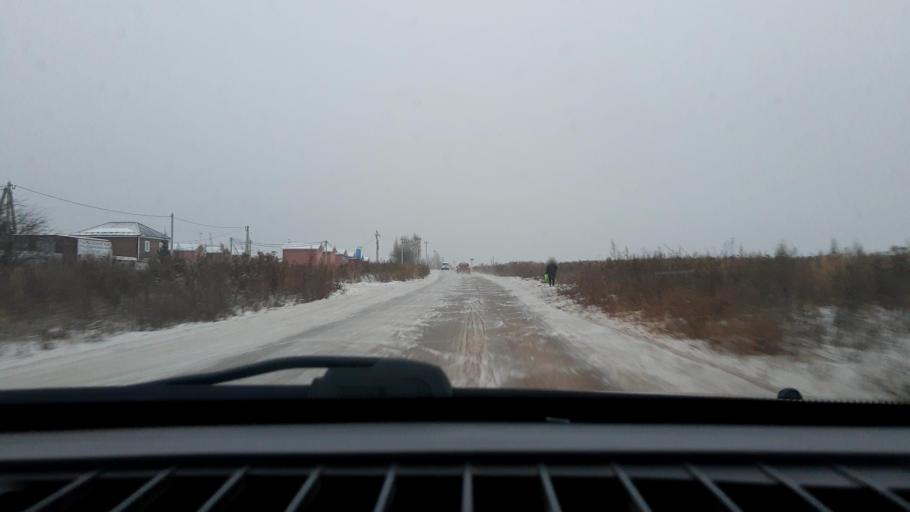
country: RU
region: Nizjnij Novgorod
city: Afonino
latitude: 56.2032
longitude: 44.0762
